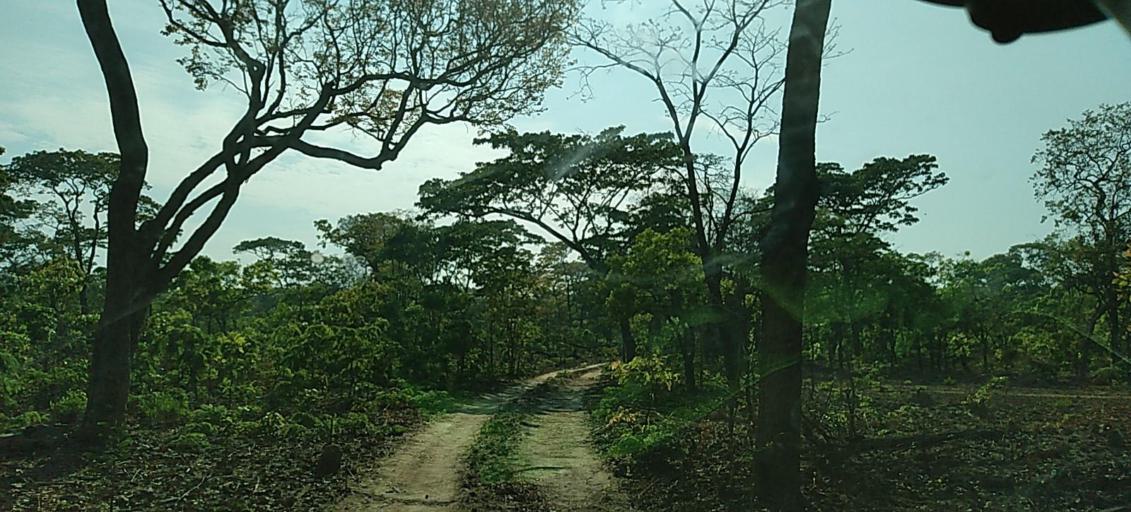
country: ZM
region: North-Western
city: Kalengwa
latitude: -13.2349
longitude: 25.0623
